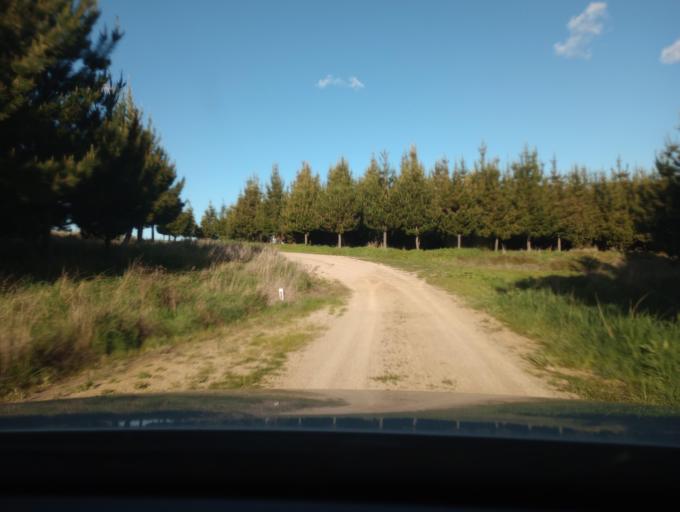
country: AU
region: New South Wales
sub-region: Blayney
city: Millthorpe
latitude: -33.3979
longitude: 149.3132
